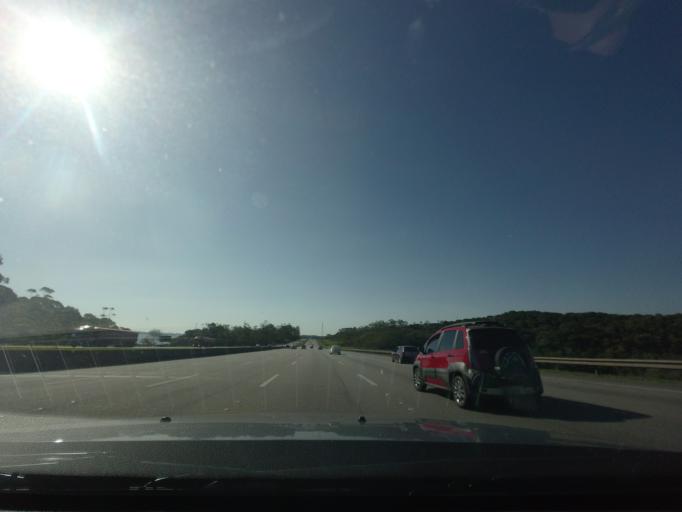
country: BR
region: Sao Paulo
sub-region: Sao Bernardo Do Campo
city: Sao Bernardo do Campo
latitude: -23.8149
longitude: -46.5840
